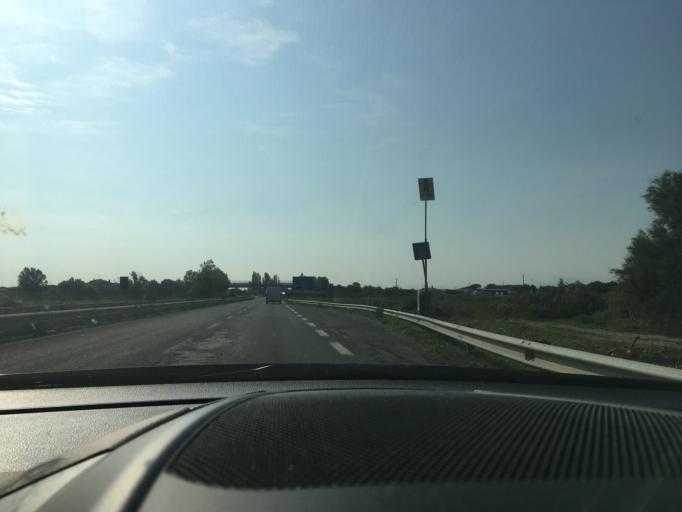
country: IT
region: Emilia-Romagna
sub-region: Forli-Cesena
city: San Mauro a Mare
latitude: 44.1531
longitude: 12.4413
